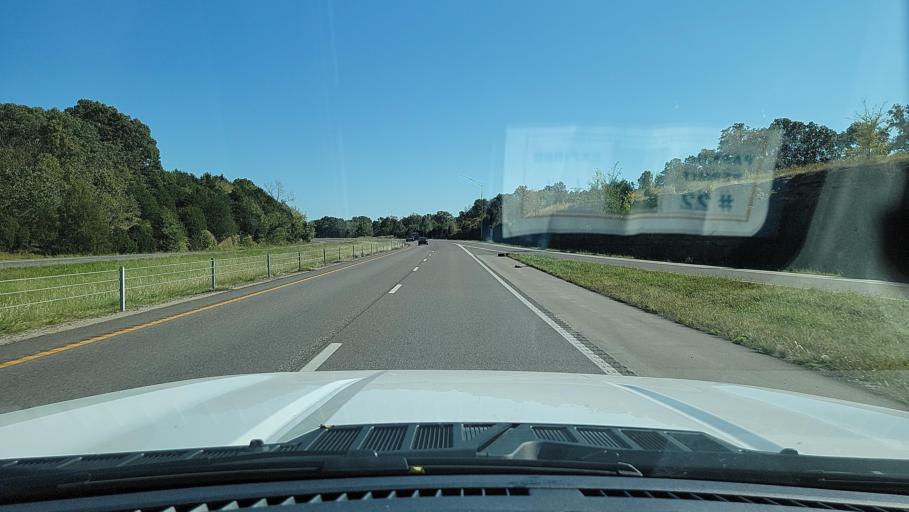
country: US
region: Missouri
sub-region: Sainte Genevieve County
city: Sainte Genevieve
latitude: 37.9716
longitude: -90.1884
